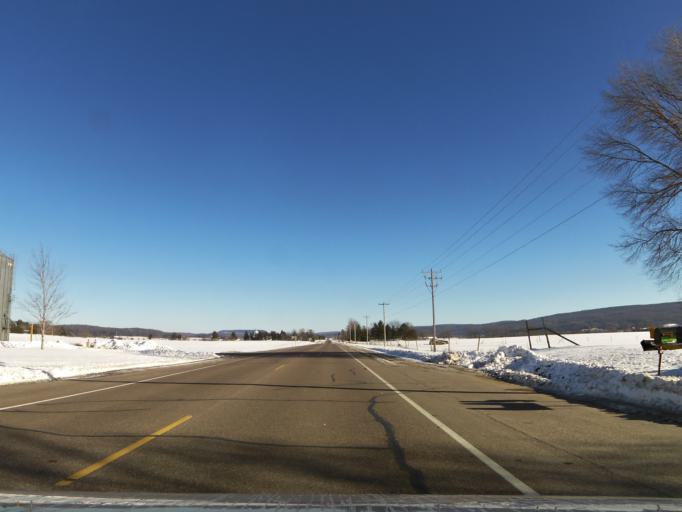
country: US
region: Wisconsin
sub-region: Sauk County
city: Baraboo
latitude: 43.4745
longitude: -89.7025
